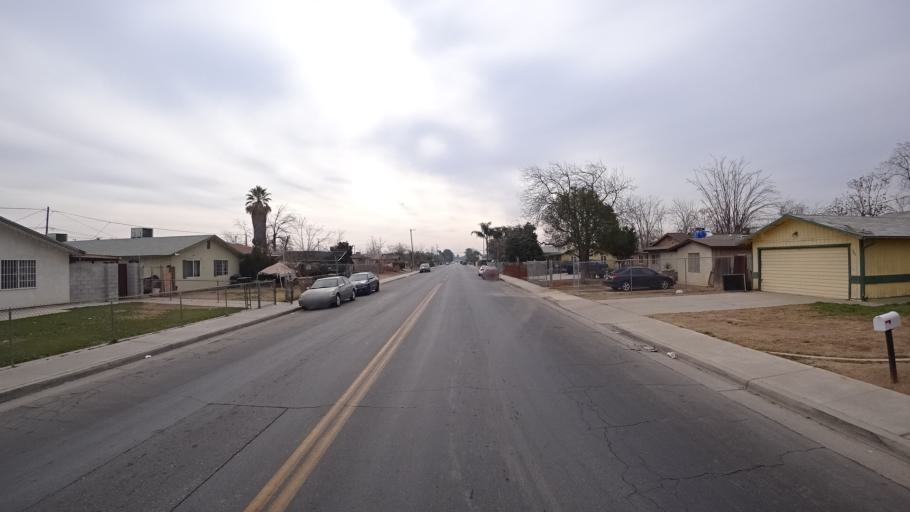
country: US
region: California
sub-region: Kern County
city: Bakersfield
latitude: 35.3609
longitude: -118.9908
